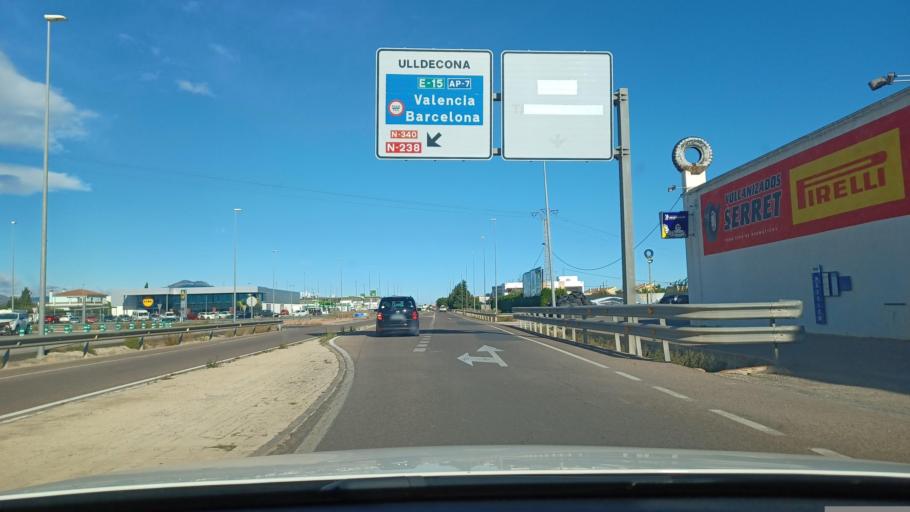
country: ES
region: Valencia
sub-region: Provincia de Castello
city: Vinaros
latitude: 40.4819
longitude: 0.4738
